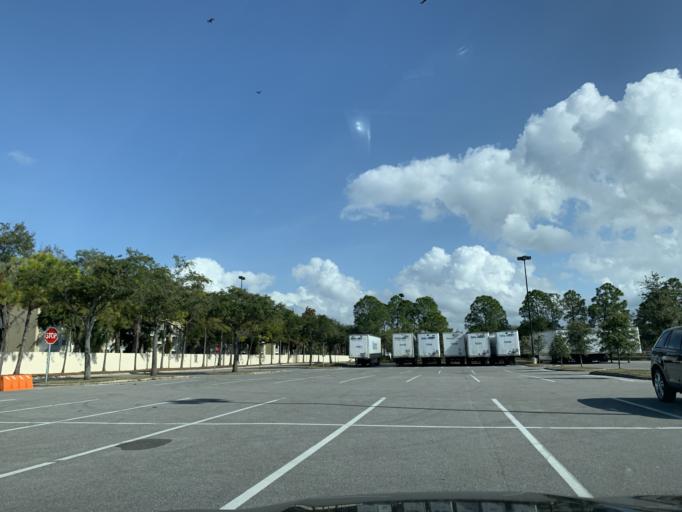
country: US
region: Florida
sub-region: Hillsborough County
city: Tampa
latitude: 27.8910
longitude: -82.5094
